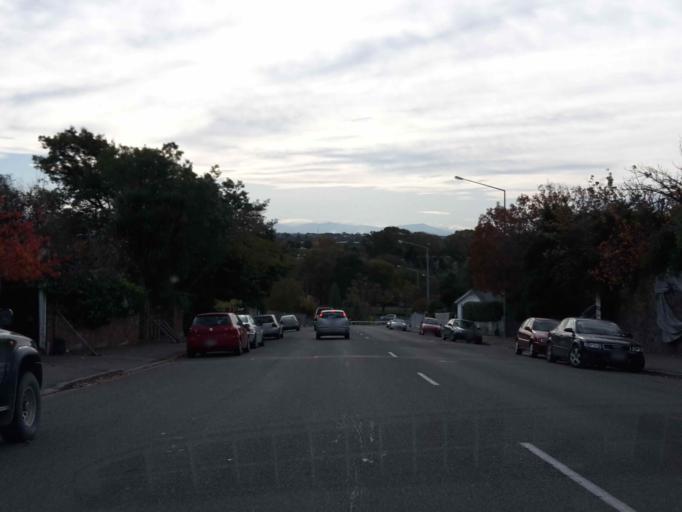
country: NZ
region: Canterbury
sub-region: Christchurch City
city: Christchurch
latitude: -43.5713
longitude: 172.6241
